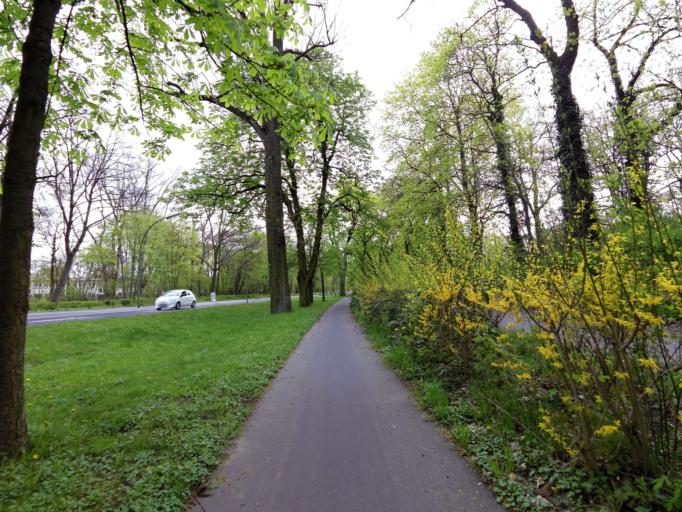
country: DE
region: Berlin
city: Britz
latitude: 52.4471
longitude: 13.4416
